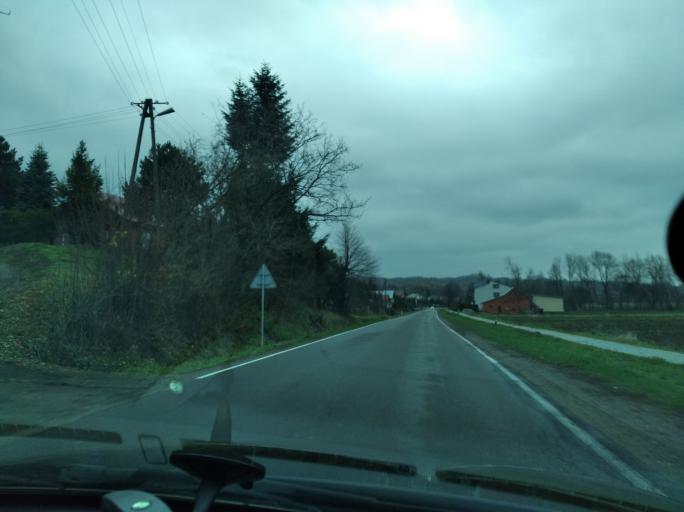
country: PL
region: Subcarpathian Voivodeship
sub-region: Powiat przeworski
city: Manasterz
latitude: 49.9285
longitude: 22.3383
